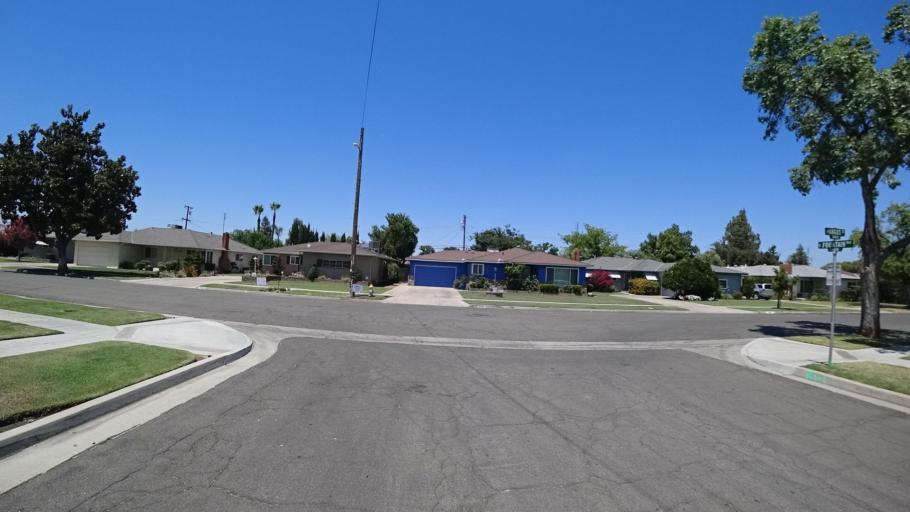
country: US
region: California
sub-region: Fresno County
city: Fresno
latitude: 36.7816
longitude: -119.7775
